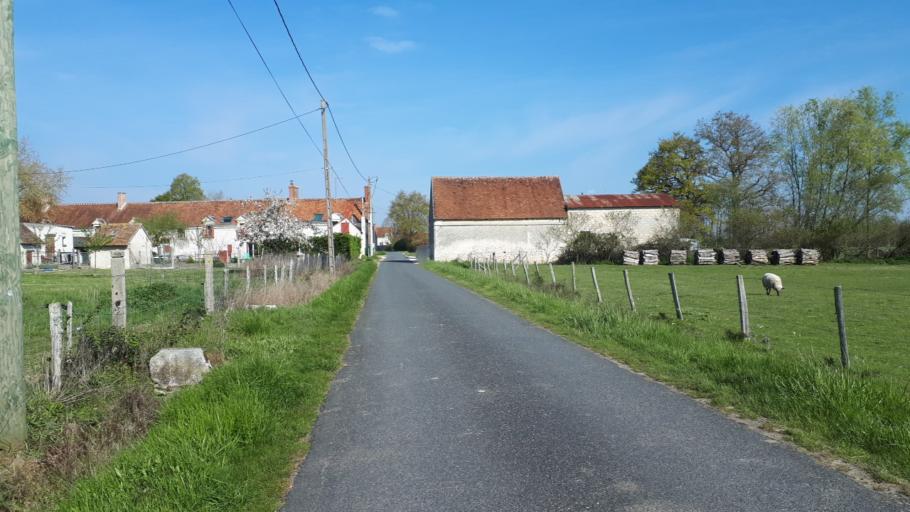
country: FR
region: Centre
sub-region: Departement du Loir-et-Cher
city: Contres
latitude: 47.3802
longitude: 1.3935
